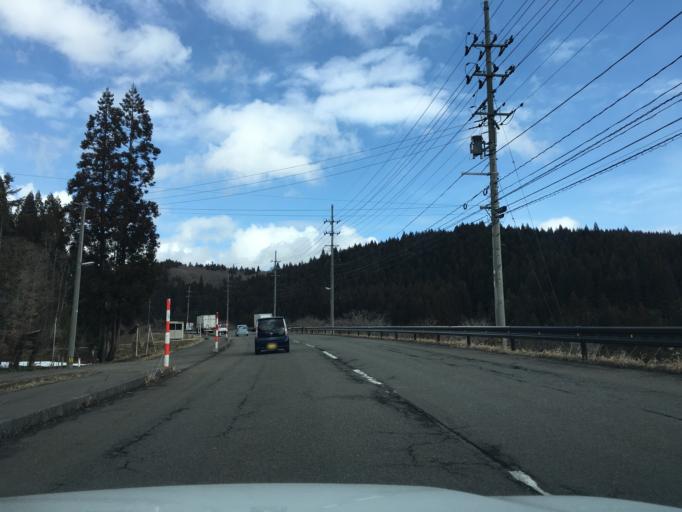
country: JP
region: Akita
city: Takanosu
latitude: 40.0924
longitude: 140.3395
